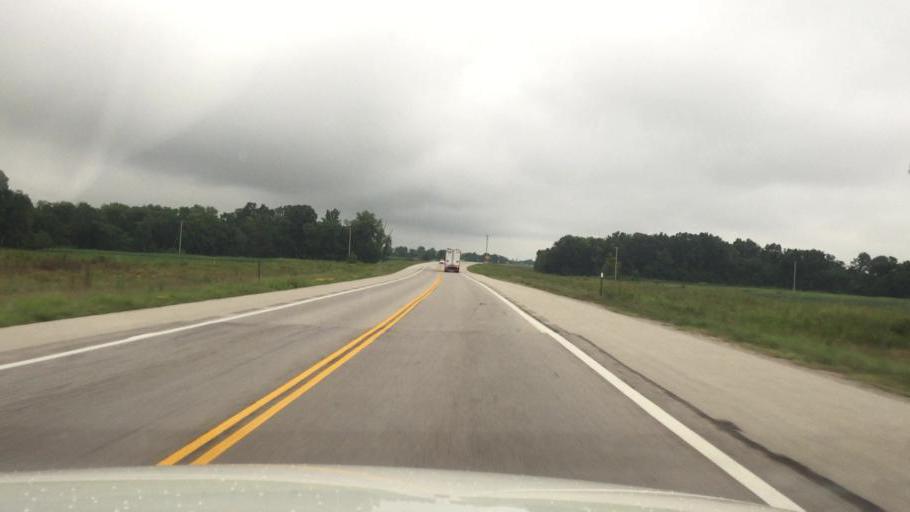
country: US
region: Kansas
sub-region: Montgomery County
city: Coffeyville
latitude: 37.1188
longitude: -95.5829
